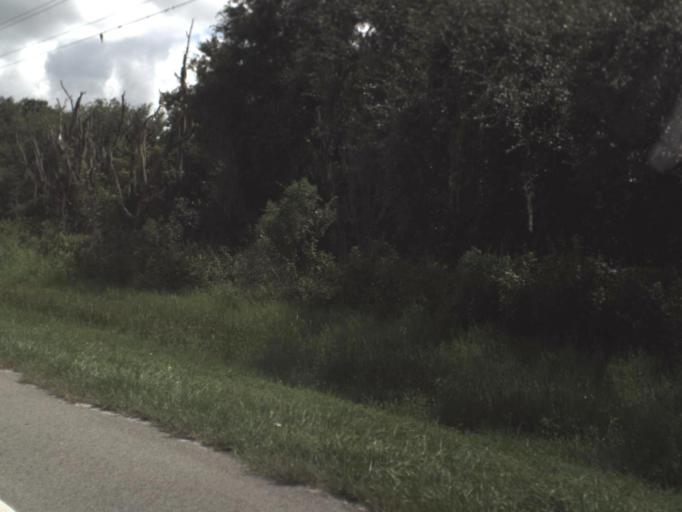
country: US
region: Florida
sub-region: Hillsborough County
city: Wimauma
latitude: 27.4621
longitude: -82.1849
